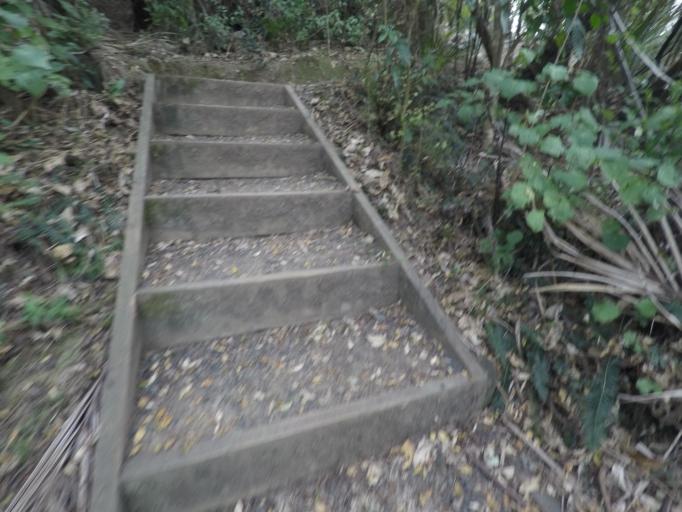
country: NZ
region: Auckland
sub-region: Auckland
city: Rothesay Bay
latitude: -36.6570
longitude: 174.7278
